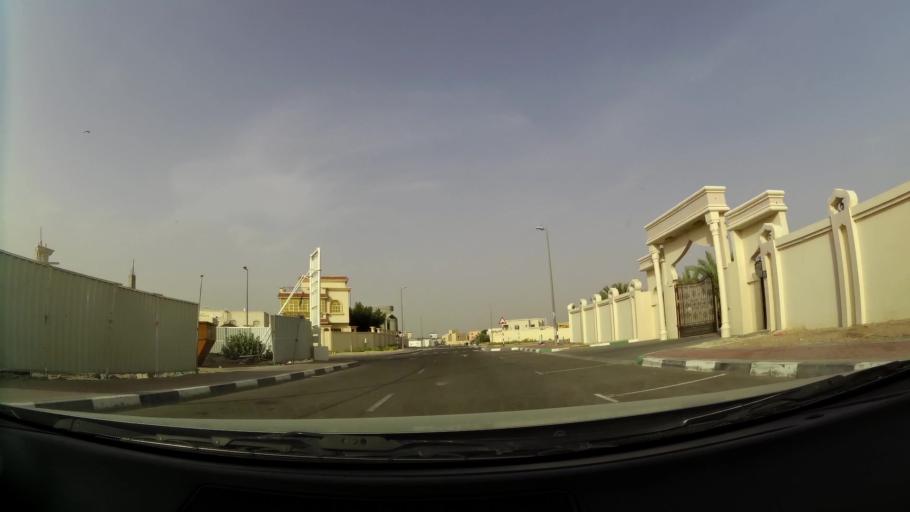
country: AE
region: Abu Dhabi
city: Al Ain
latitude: 24.1202
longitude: 55.6959
